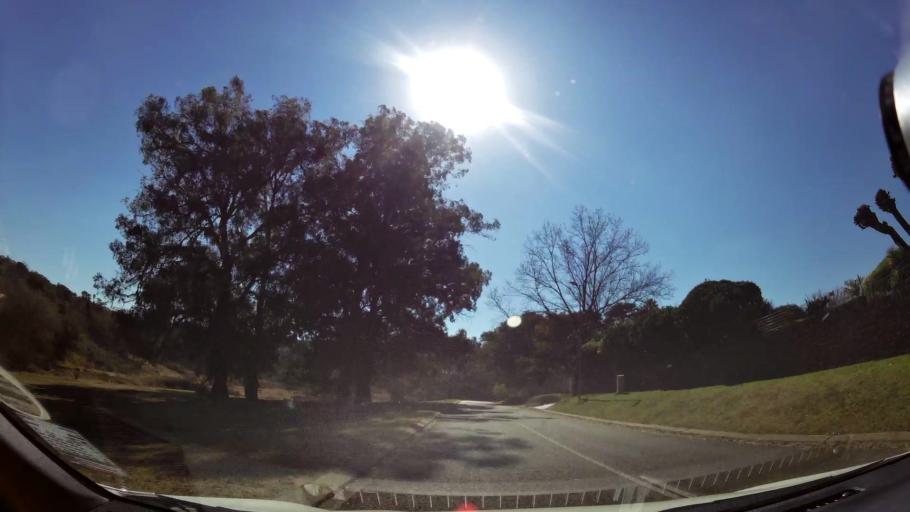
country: ZA
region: Gauteng
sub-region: City of Johannesburg Metropolitan Municipality
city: Johannesburg
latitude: -26.2714
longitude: 28.0100
